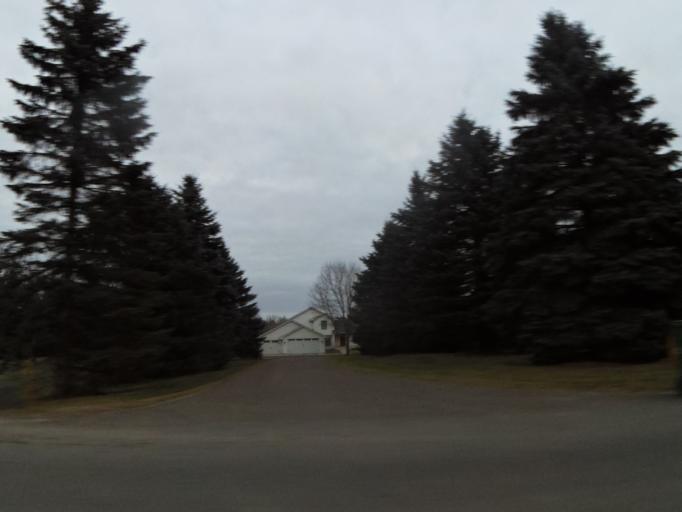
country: US
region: Minnesota
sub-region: Washington County
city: Grant
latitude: 45.0583
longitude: -92.8834
